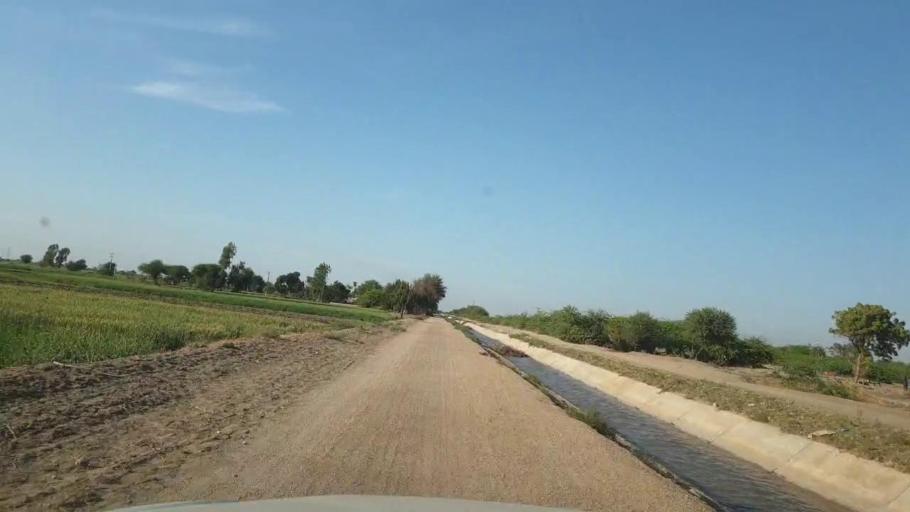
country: PK
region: Sindh
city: Kunri
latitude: 25.0931
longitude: 69.4285
